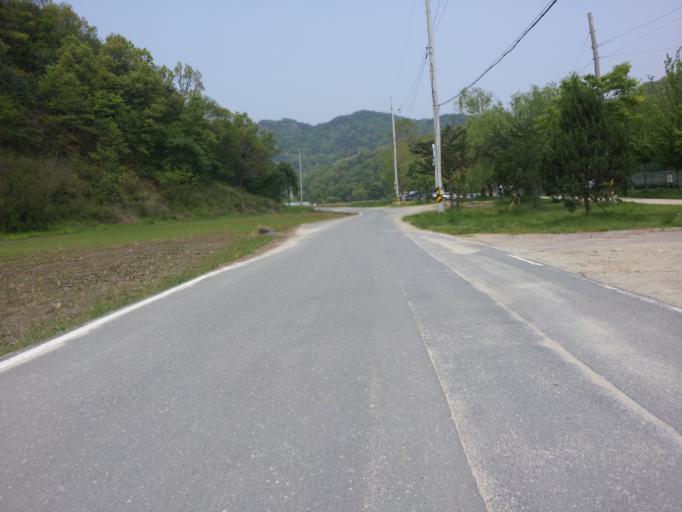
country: KR
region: Daejeon
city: Daejeon
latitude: 36.2758
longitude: 127.3437
